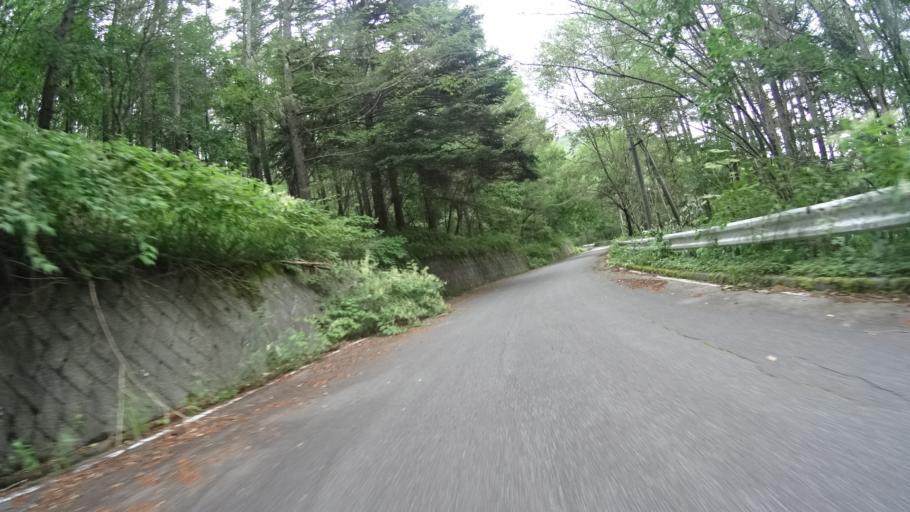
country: JP
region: Yamanashi
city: Enzan
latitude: 35.7990
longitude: 138.6373
